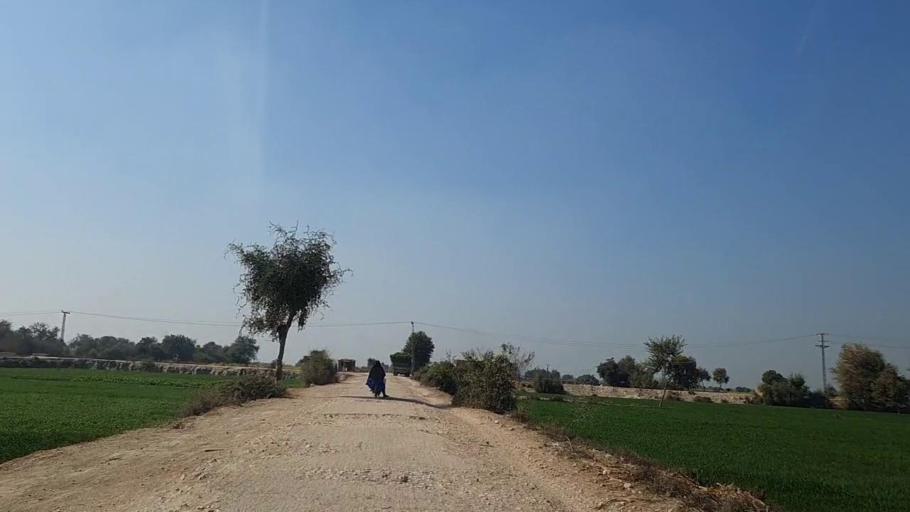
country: PK
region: Sindh
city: Daulatpur
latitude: 26.2906
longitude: 68.0809
